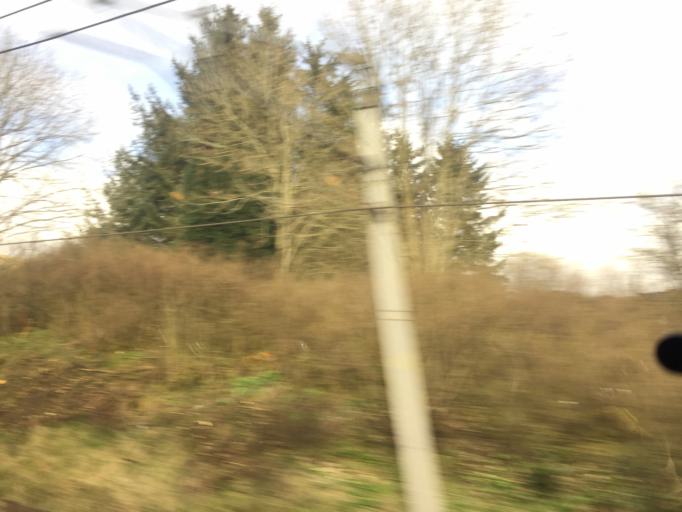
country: GB
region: Scotland
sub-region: South Lanarkshire
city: Biggar
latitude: 55.4710
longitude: -3.6539
